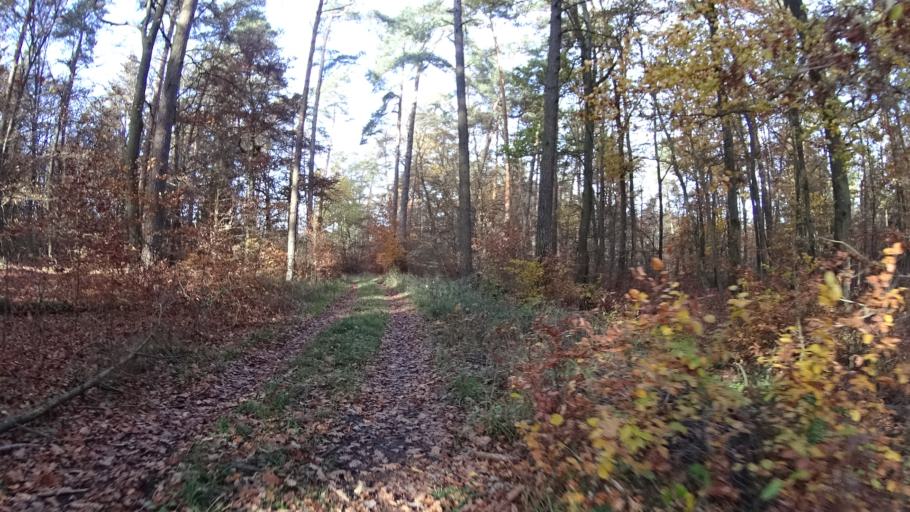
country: DE
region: Rheinland-Pfalz
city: Unterjeckenbach
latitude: 49.6775
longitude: 7.4824
